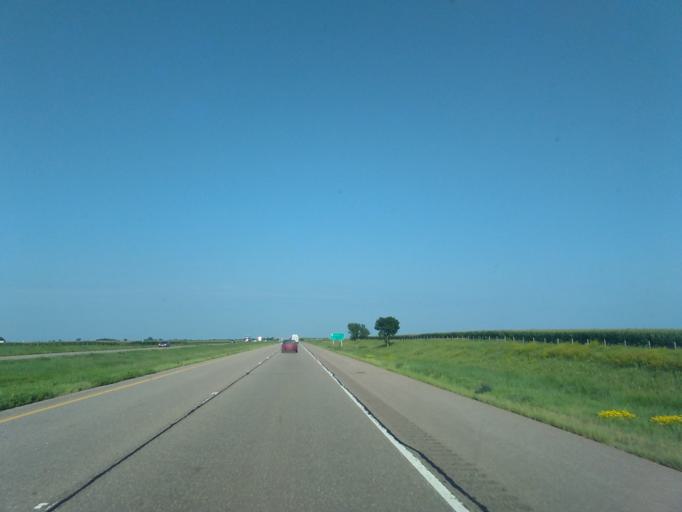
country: US
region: Nebraska
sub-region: Hamilton County
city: Aurora
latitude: 40.8220
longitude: -98.1358
